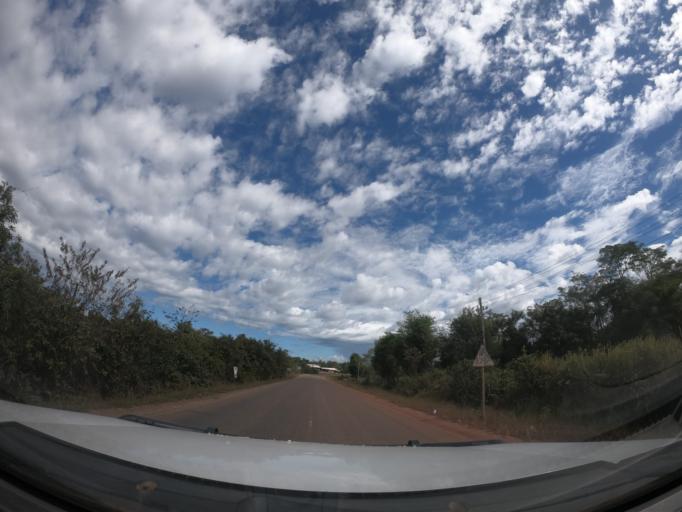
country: LA
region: Bolikhamxai
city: Muang Pakxan
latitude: 18.4361
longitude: 103.5508
